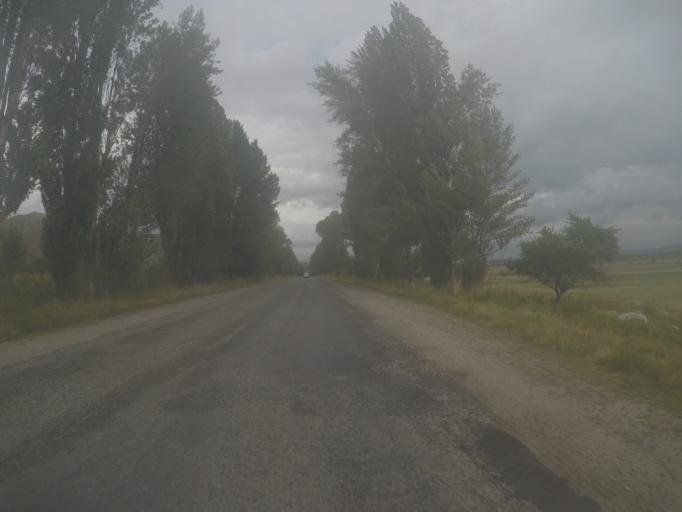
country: KG
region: Ysyk-Koel
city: Tyup
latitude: 42.7429
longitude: 78.0667
